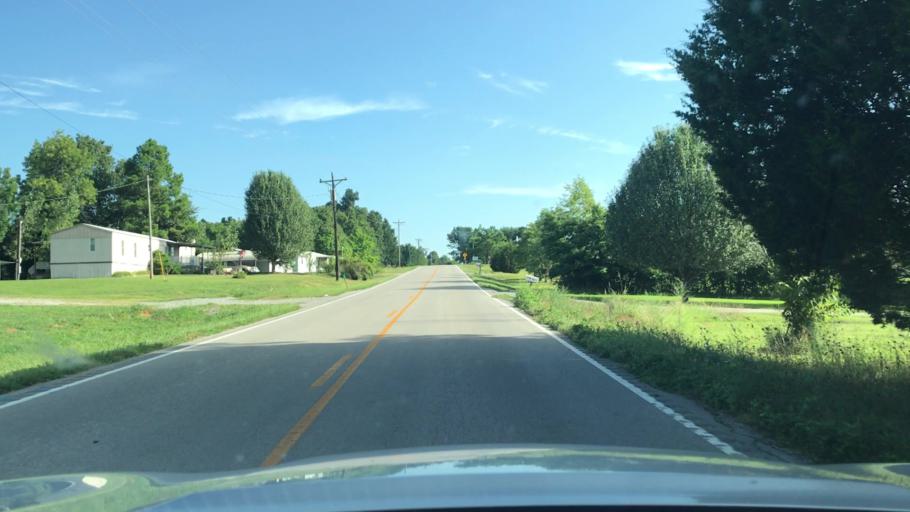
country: US
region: Kentucky
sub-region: Todd County
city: Elkton
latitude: 36.9266
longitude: -87.1624
